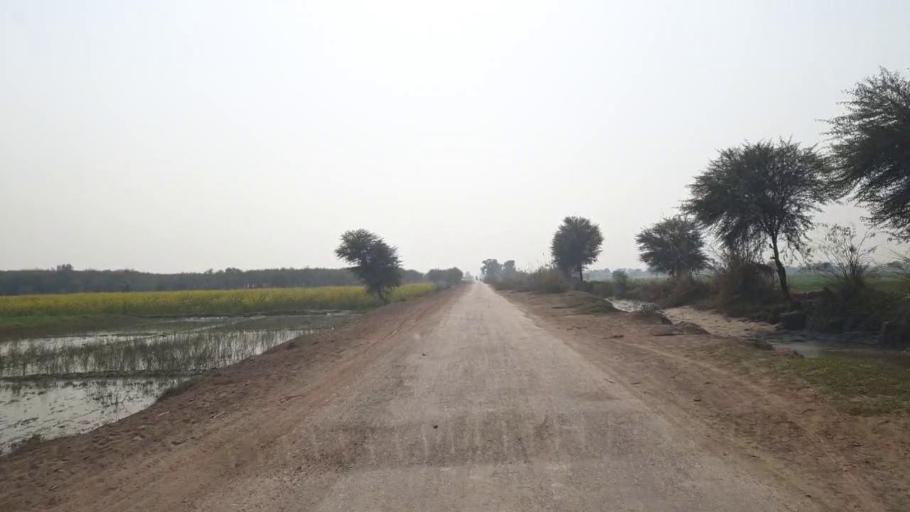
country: PK
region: Sindh
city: Hala
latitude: 25.9176
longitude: 68.4459
